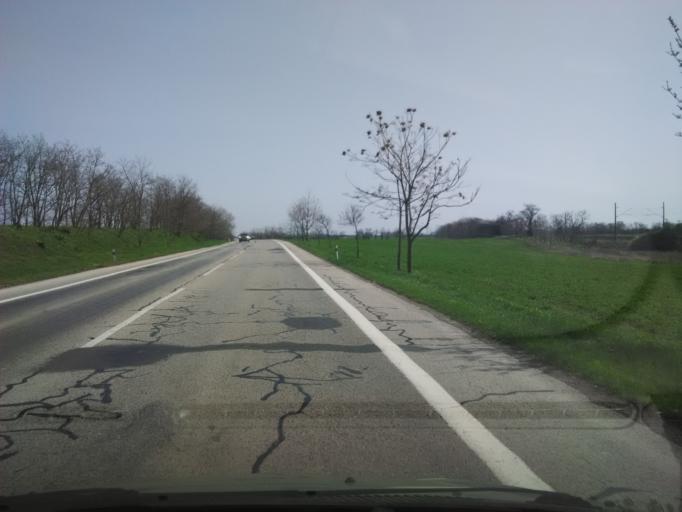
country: SK
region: Nitriansky
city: Sellye
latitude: 48.1457
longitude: 17.9714
